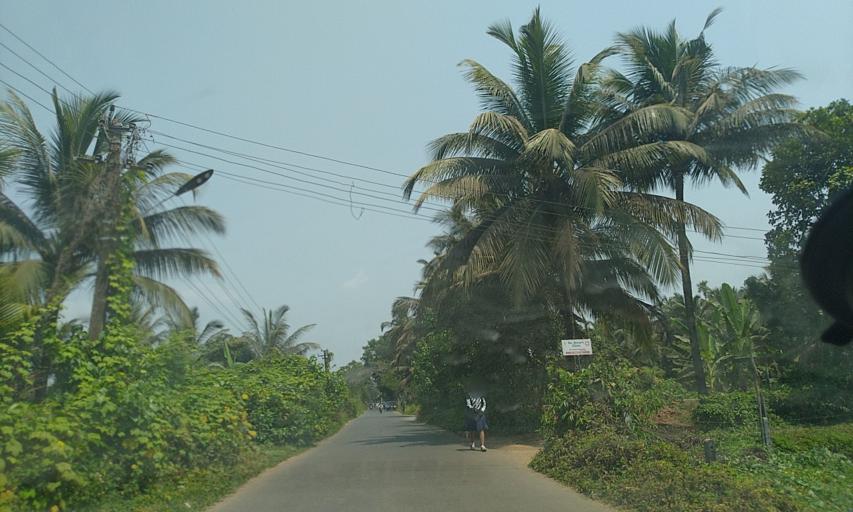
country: IN
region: Goa
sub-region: North Goa
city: Guirim
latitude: 15.5531
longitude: 73.8146
